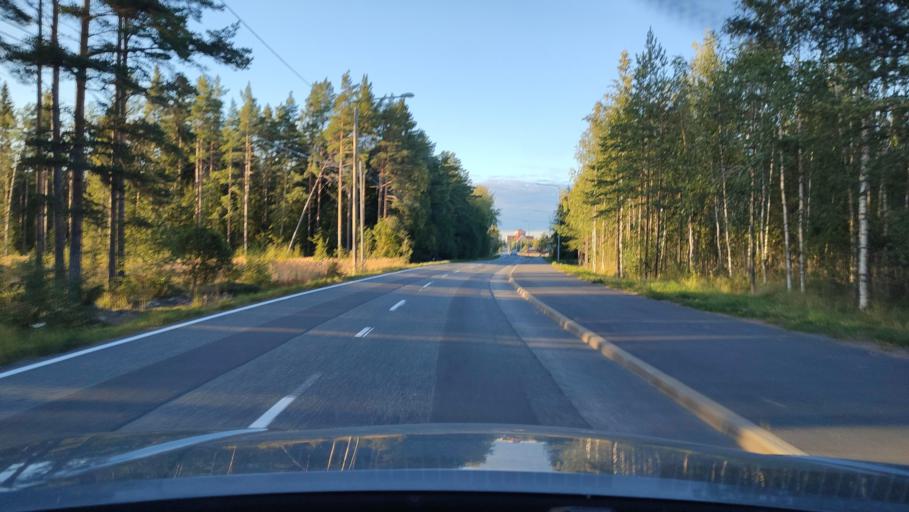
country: FI
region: Ostrobothnia
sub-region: Sydosterbotten
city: Kristinestad
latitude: 62.2359
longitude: 21.5209
